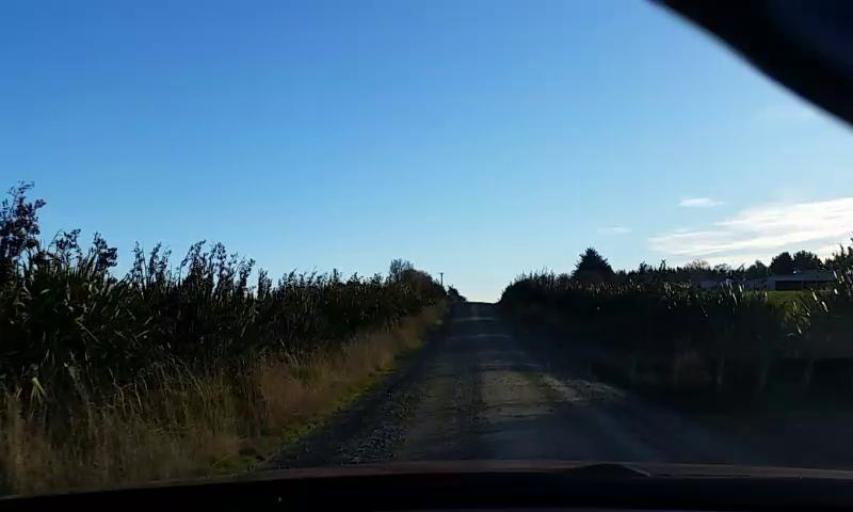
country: NZ
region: Southland
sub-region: Invercargill City
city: Invercargill
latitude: -46.2850
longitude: 168.5162
